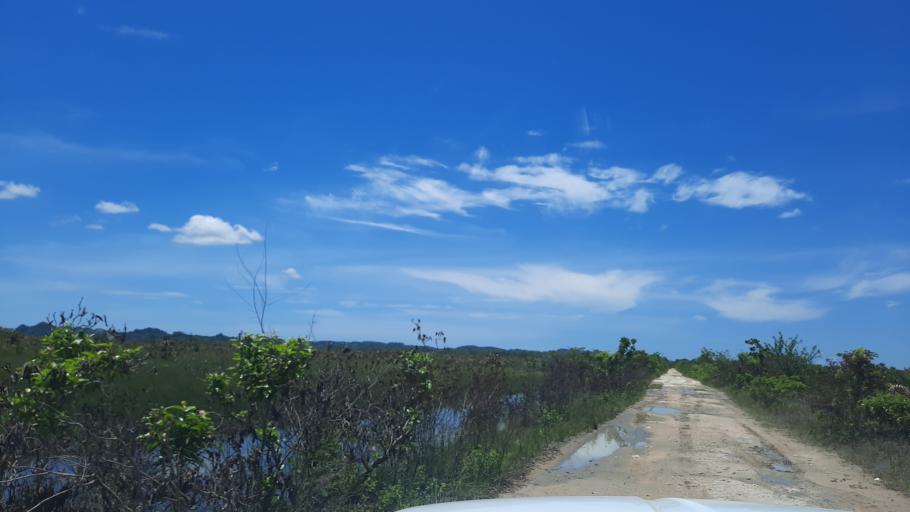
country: BZ
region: Cayo
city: Belmopan
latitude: 17.3835
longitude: -88.4938
